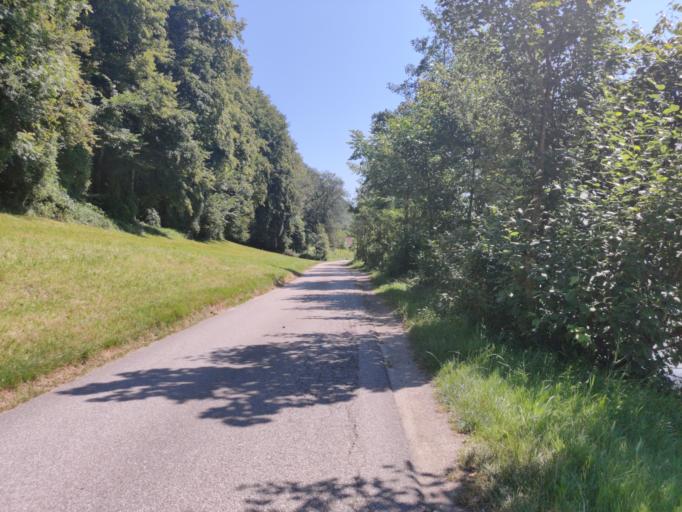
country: AT
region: Upper Austria
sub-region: Politischer Bezirk Rohrbach
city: Pfarrkirchen im Muehlkreis
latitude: 48.4570
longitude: 13.8192
